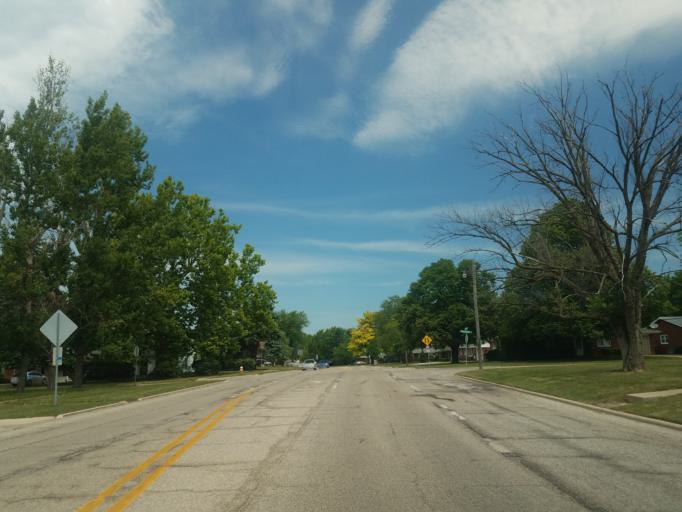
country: US
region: Illinois
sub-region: McLean County
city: Bloomington
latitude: 40.4892
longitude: -88.9611
